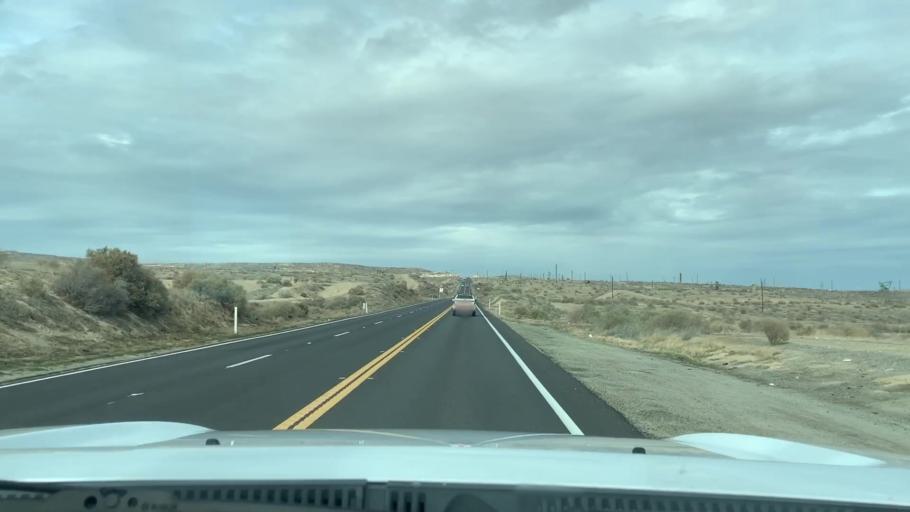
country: US
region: California
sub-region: Kern County
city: South Taft
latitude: 35.1081
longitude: -119.4226
